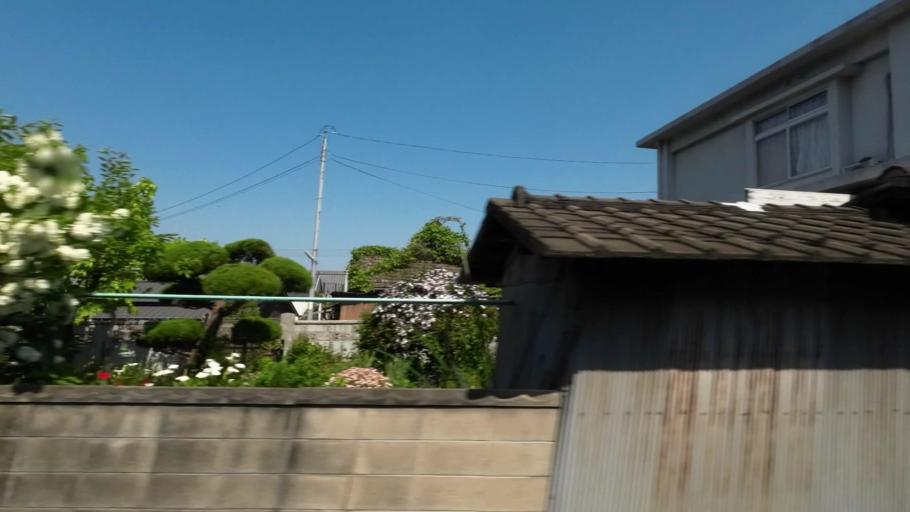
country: JP
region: Ehime
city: Kawanoecho
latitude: 34.0305
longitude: 133.5854
